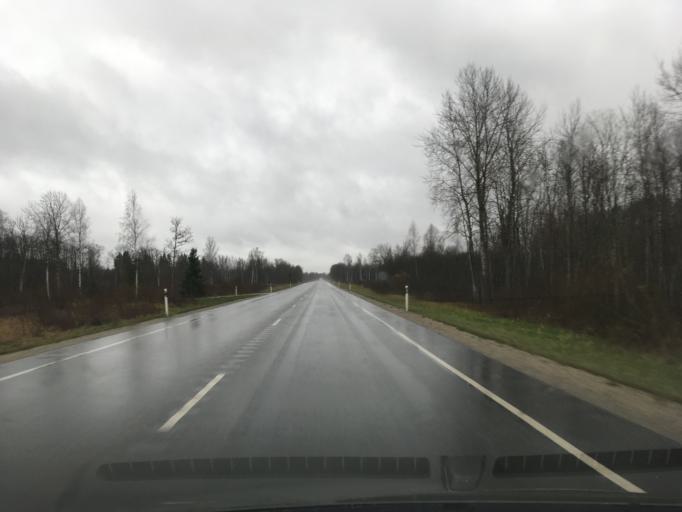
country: EE
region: Laeaene
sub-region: Lihula vald
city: Lihula
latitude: 58.8056
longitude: 24.0489
